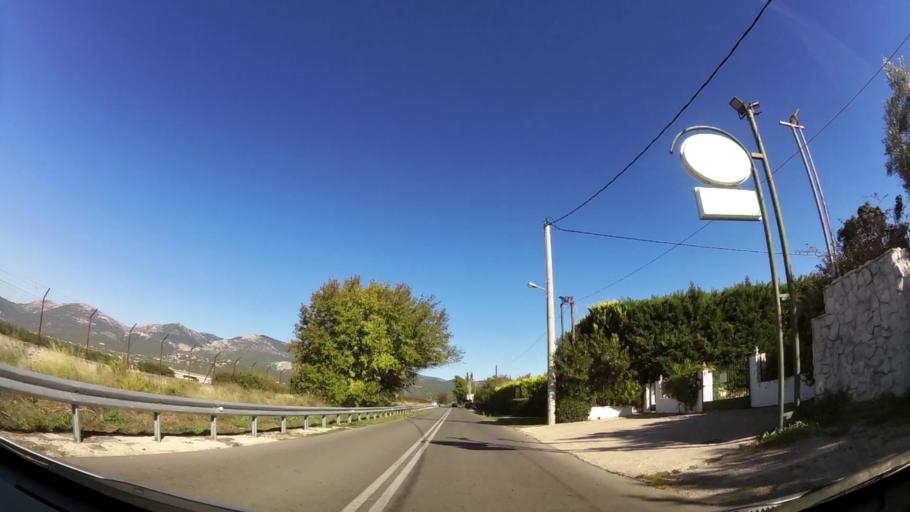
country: GR
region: Attica
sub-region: Nomarchia Anatolikis Attikis
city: Varybobi
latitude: 38.1129
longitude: 23.7899
